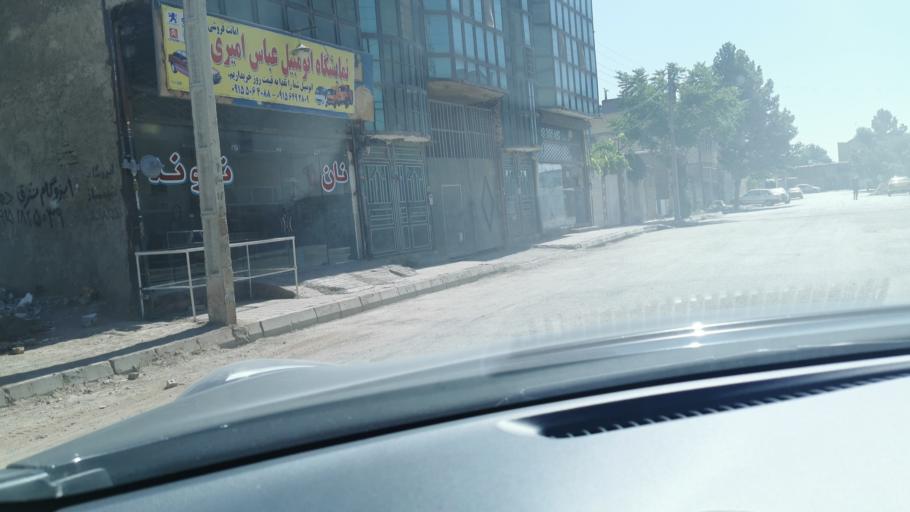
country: IR
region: Razavi Khorasan
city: Chenaran
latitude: 36.6398
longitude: 59.1163
